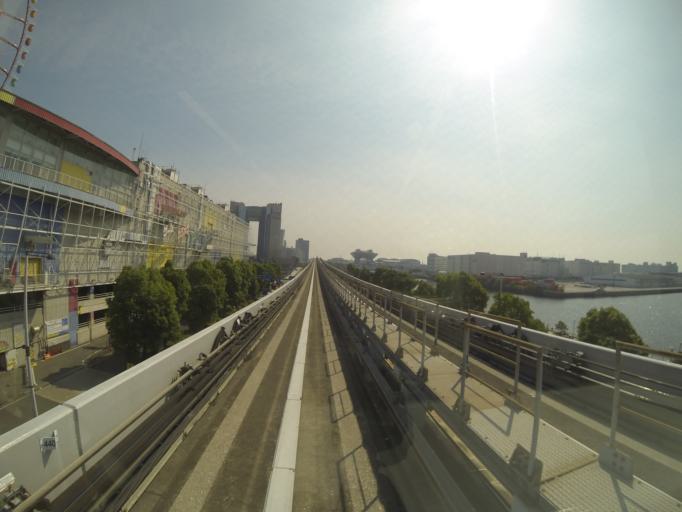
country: JP
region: Tokyo
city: Tokyo
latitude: 35.6255
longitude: 139.7825
